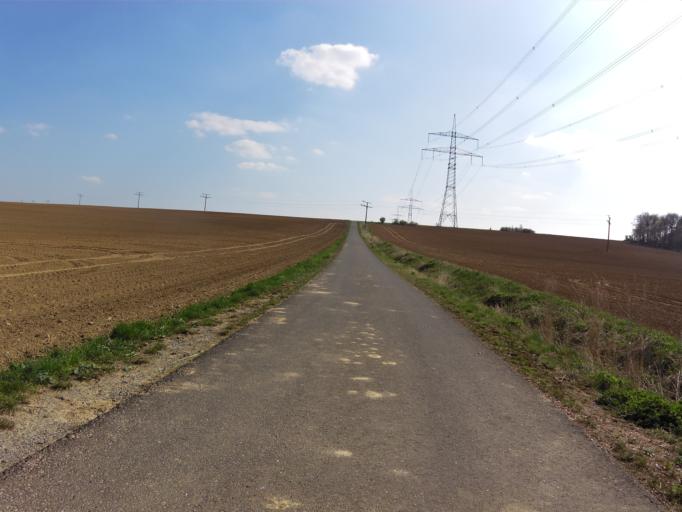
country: DE
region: Bavaria
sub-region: Regierungsbezirk Unterfranken
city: Rottendorf
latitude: 49.7780
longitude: 10.0504
